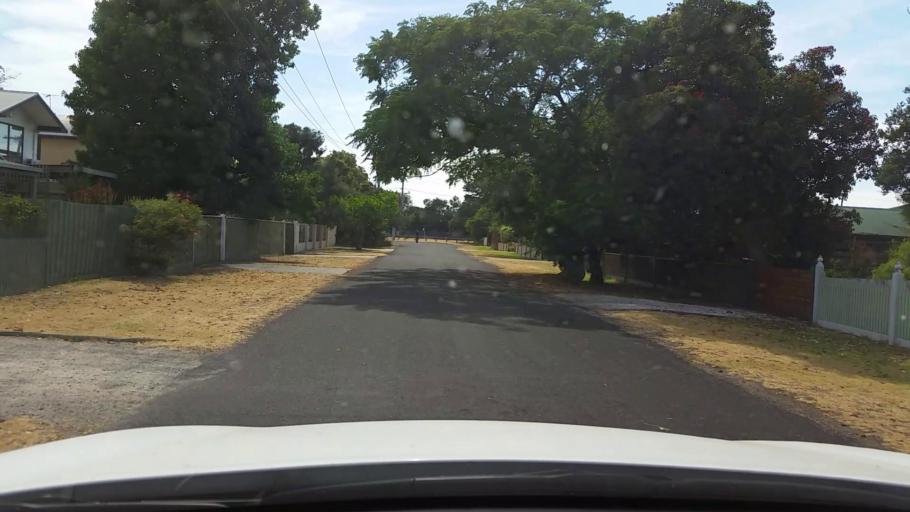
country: AU
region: Victoria
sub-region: Mornington Peninsula
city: Rosebud West
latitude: -38.3672
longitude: 144.8703
